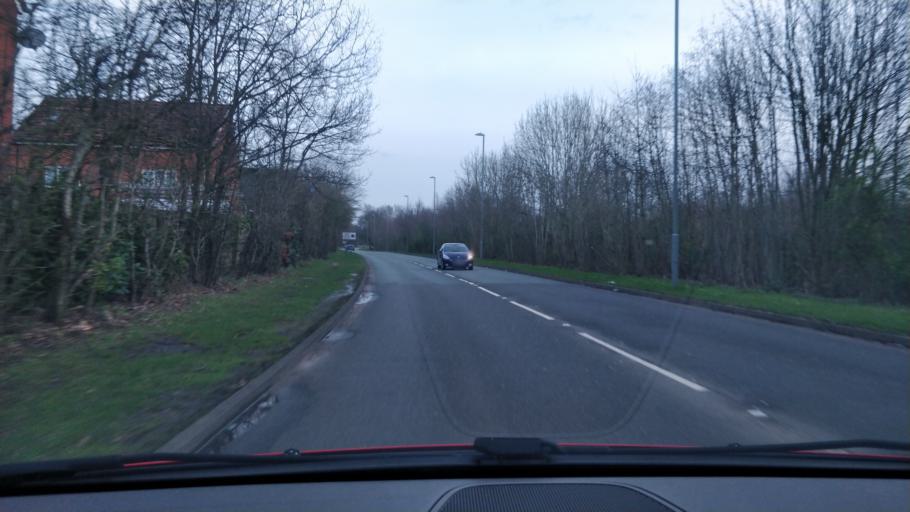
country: GB
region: England
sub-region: Knowsley
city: Huyton
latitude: 53.4286
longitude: -2.8546
